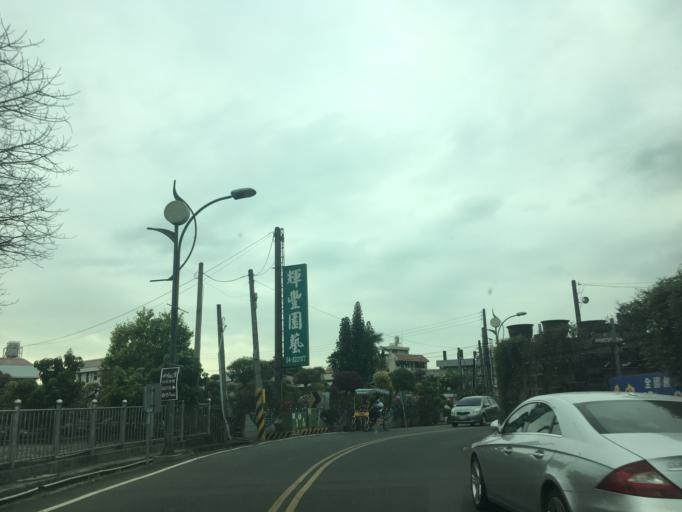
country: TW
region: Taiwan
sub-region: Nantou
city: Nantou
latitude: 23.9021
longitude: 120.5307
